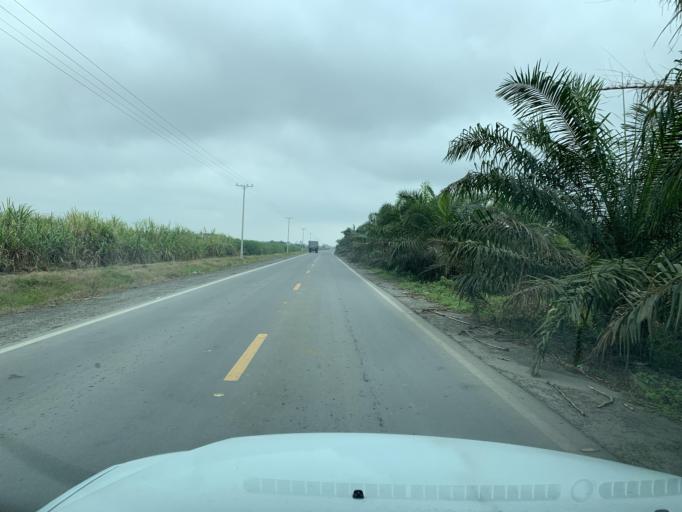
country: EC
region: Guayas
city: Coronel Marcelino Mariduena
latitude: -2.3195
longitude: -79.5175
